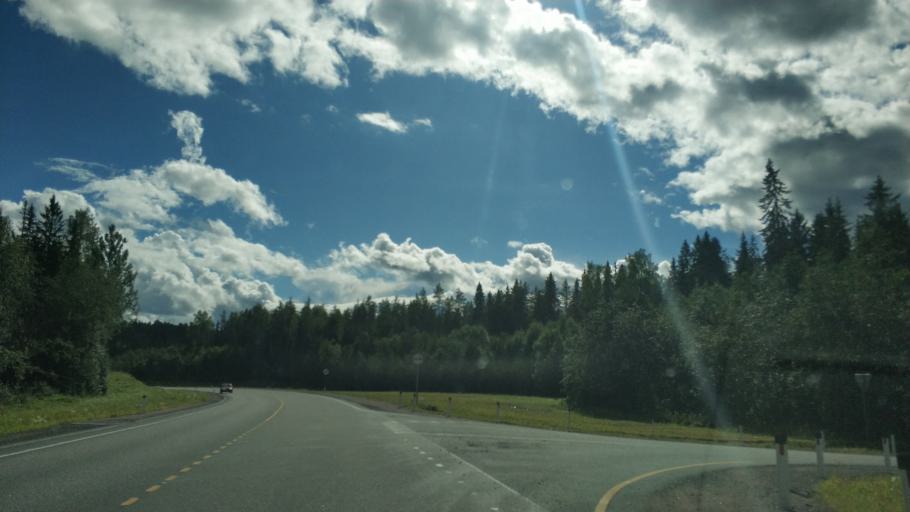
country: RU
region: Republic of Karelia
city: Ruskeala
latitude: 61.9129
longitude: 30.6265
